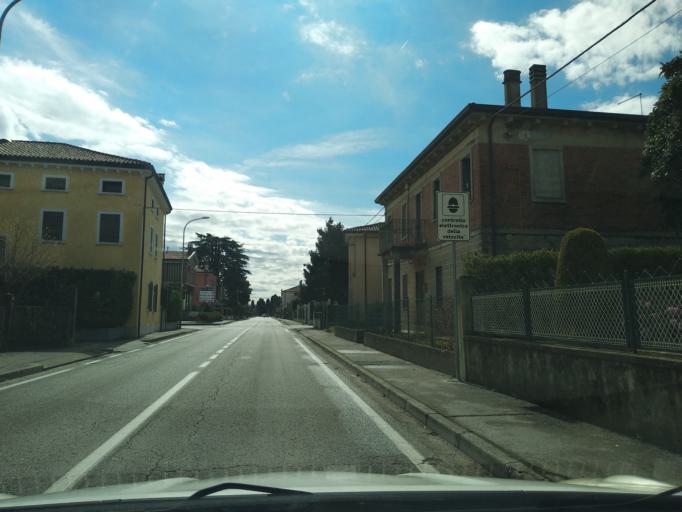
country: IT
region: Veneto
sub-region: Provincia di Vicenza
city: Monticello Conte Otto
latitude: 45.5999
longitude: 11.5730
